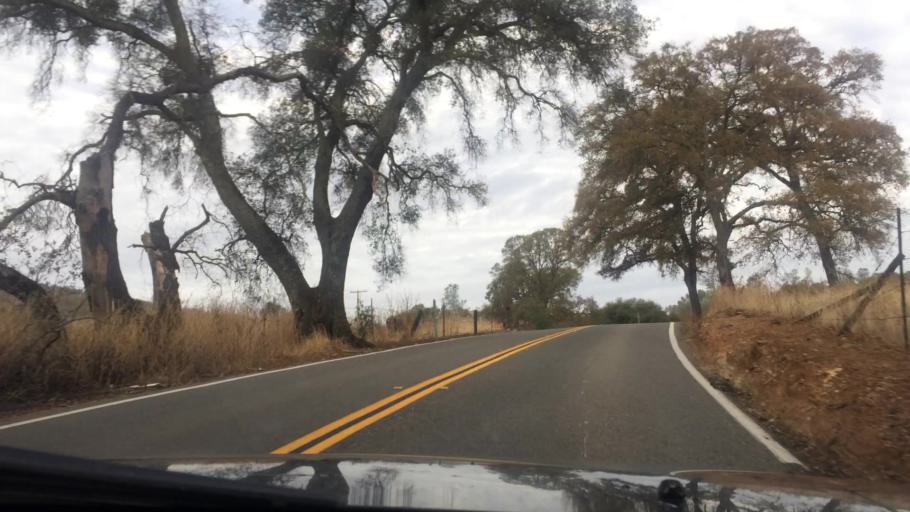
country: US
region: California
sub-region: El Dorado County
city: Cameron Park
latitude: 38.5858
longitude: -121.0083
